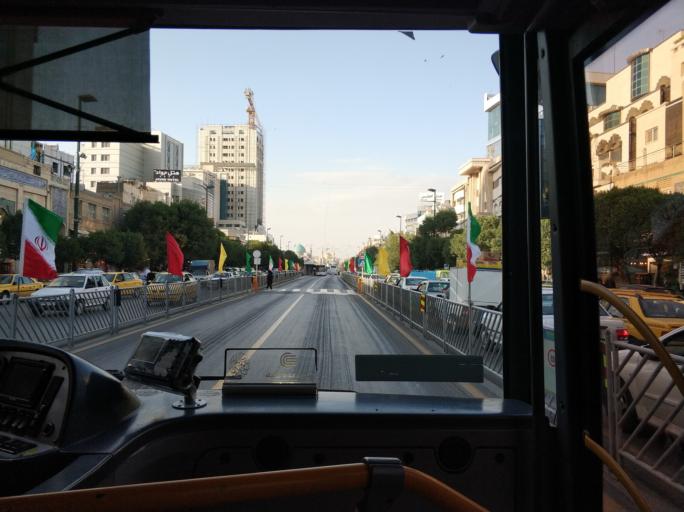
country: IR
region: Razavi Khorasan
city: Mashhad
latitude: 36.2813
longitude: 59.6101
